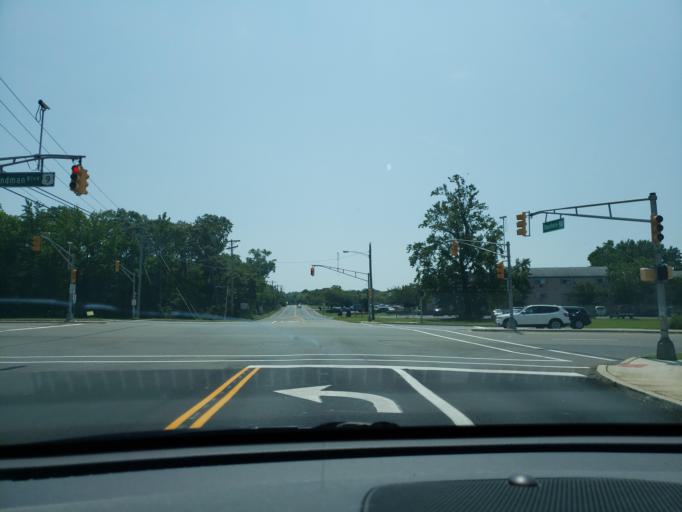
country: US
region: New Jersey
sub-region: Cape May County
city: North Cape May
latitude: 38.9735
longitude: -74.9424
